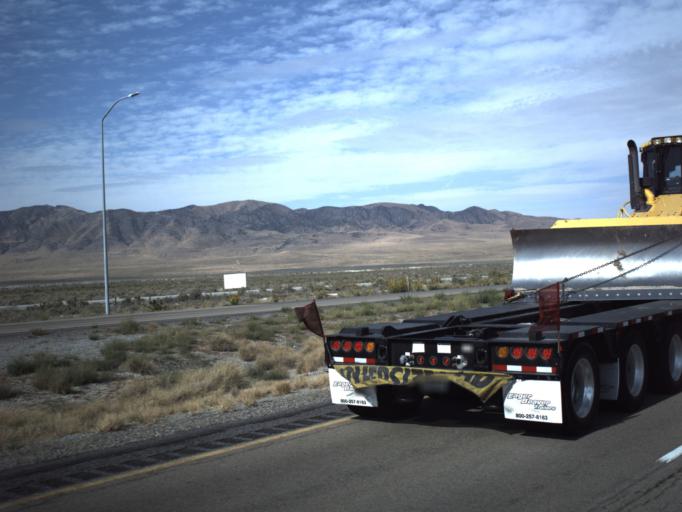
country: US
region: Utah
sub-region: Tooele County
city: Grantsville
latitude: 40.7655
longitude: -112.7860
